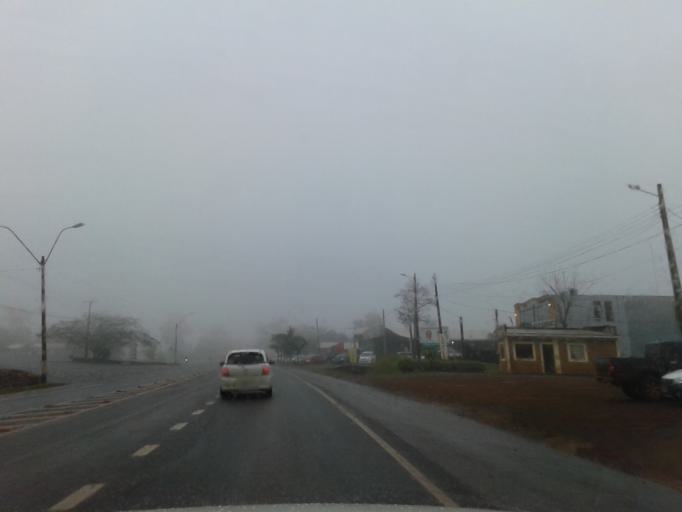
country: PY
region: Itapua
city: Arquitecto Tomas Romero Pereira
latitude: -26.5461
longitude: -55.2565
